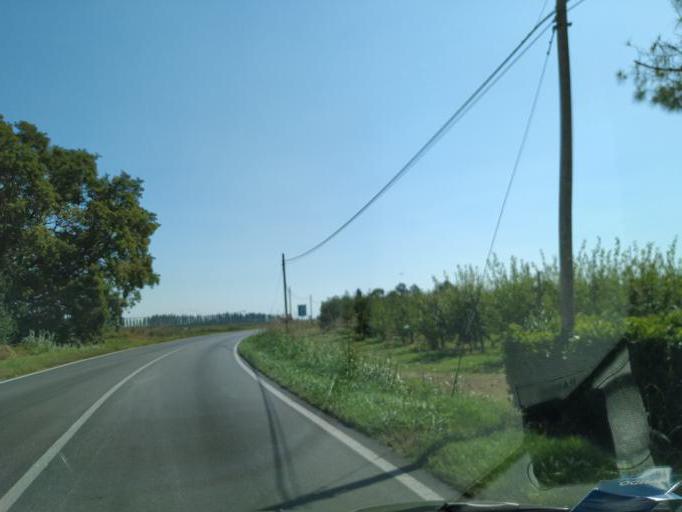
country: IT
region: Emilia-Romagna
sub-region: Provincia di Ferrara
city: Coccanile-Cesta
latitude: 44.8847
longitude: 11.8686
